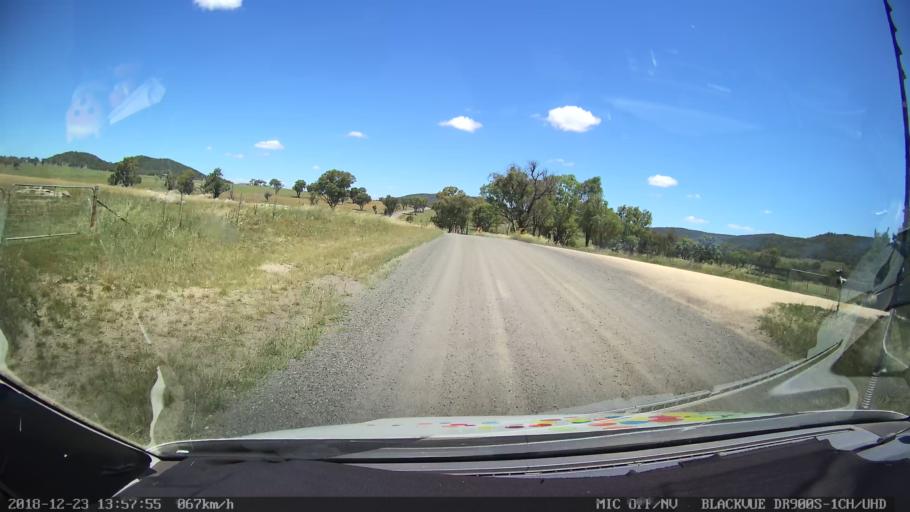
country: AU
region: New South Wales
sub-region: Tamworth Municipality
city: Manilla
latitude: -30.5934
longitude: 151.0932
